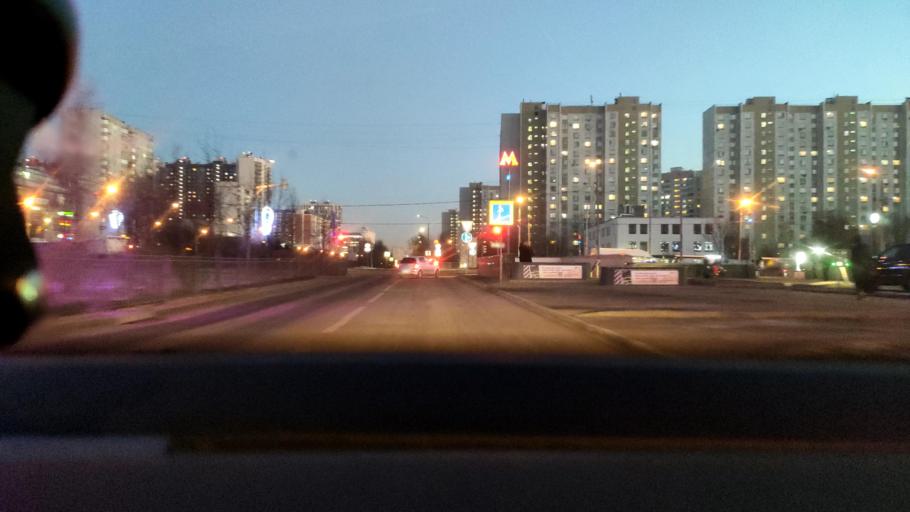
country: RU
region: Moskovskaya
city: Pavshino
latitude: 55.8467
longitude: 37.3589
